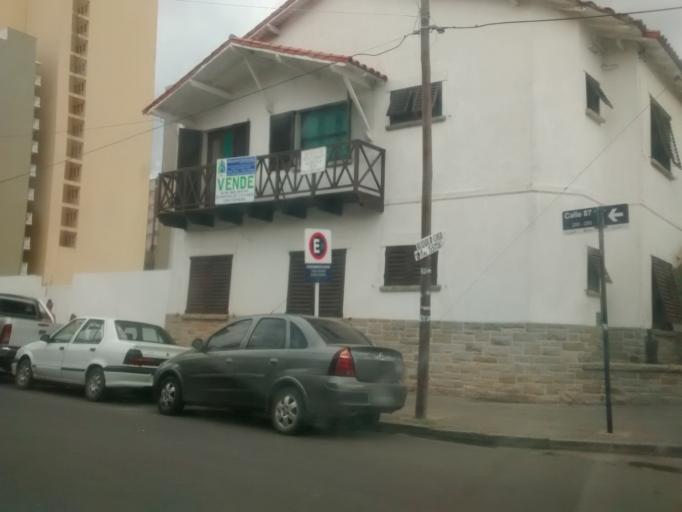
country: AR
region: Buenos Aires
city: Necochea
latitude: -38.5829
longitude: -58.7320
